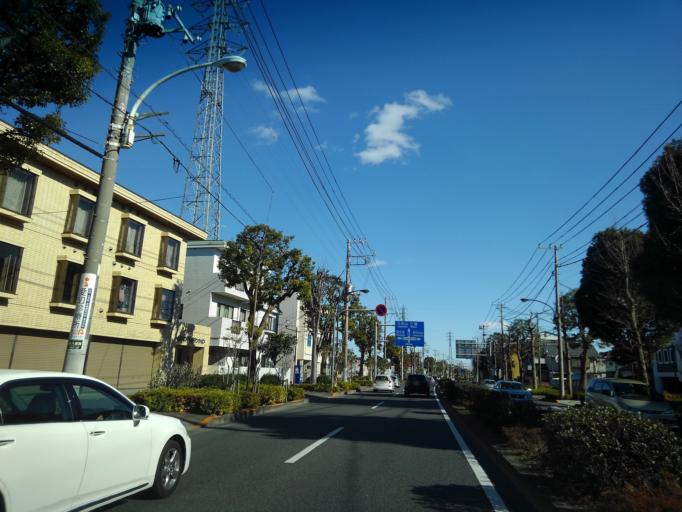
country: JP
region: Tokyo
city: Kokubunji
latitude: 35.6883
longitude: 139.4739
